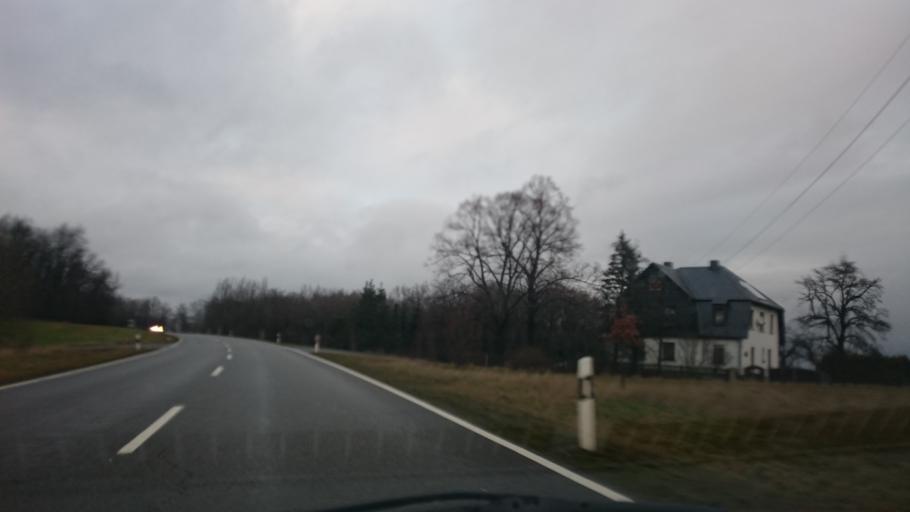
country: DE
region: Saxony
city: Lichtenstein
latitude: 50.7525
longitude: 12.6023
